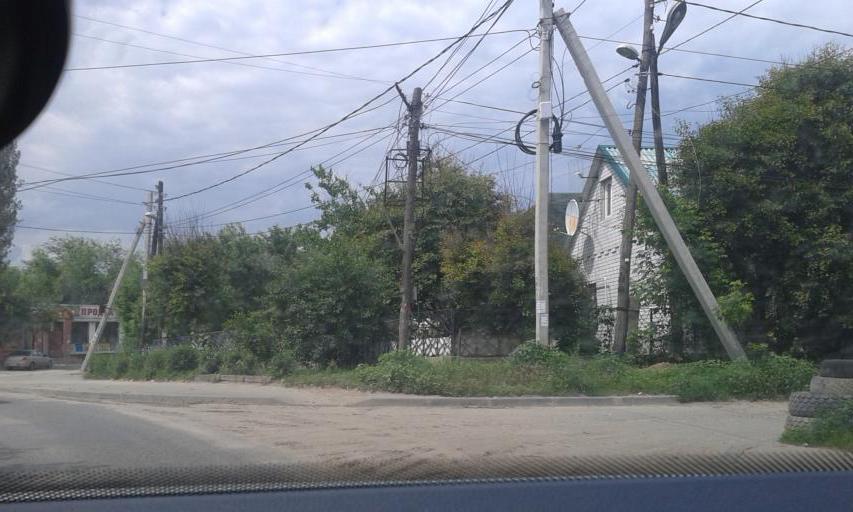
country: RU
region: Volgograd
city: Gorodishche
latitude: 48.7726
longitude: 44.4946
